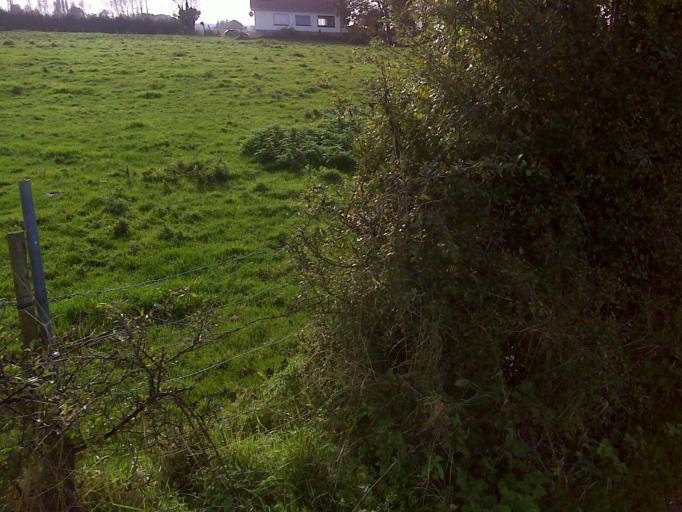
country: FR
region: Nord-Pas-de-Calais
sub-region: Departement du Nord
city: Winnezeele
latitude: 50.8618
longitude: 2.5937
